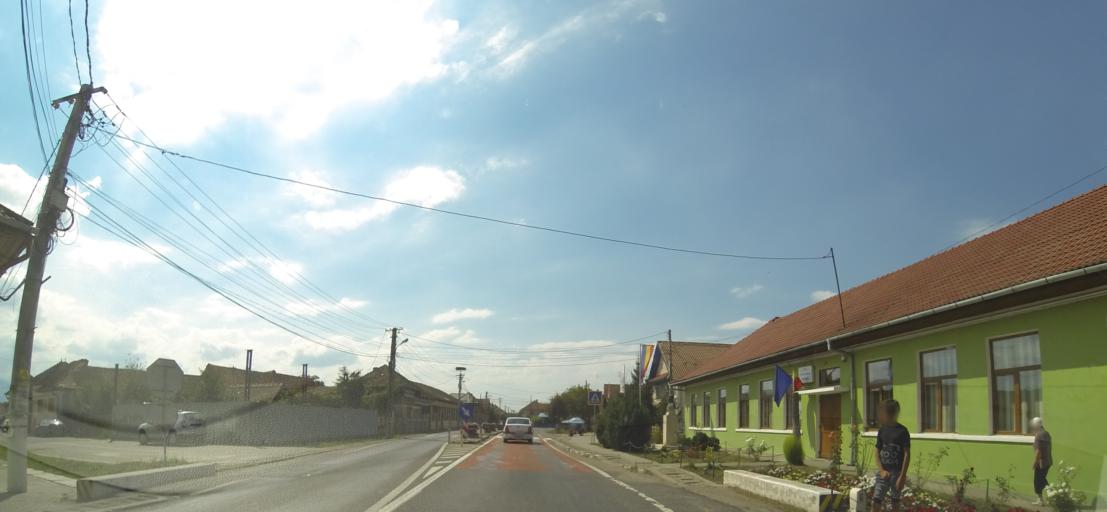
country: RO
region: Brasov
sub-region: Comuna Mandra
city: Mandra
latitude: 45.8226
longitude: 25.0475
